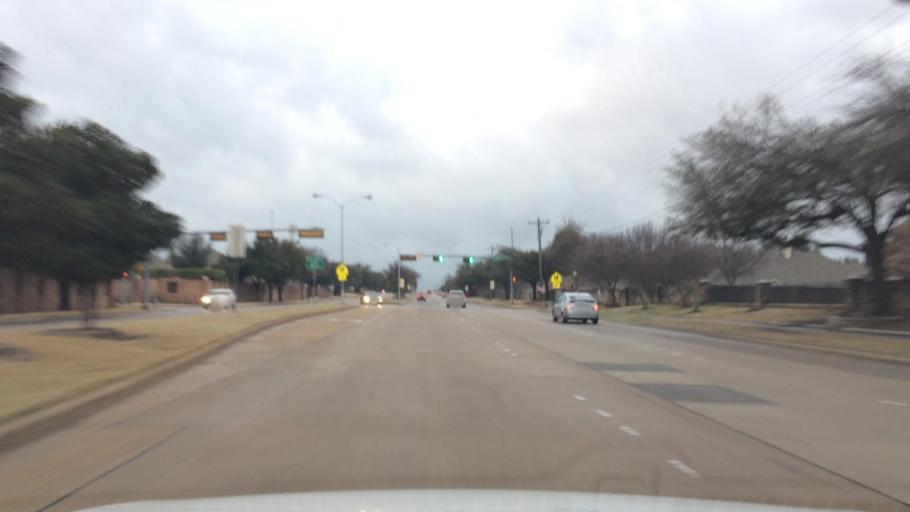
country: US
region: Texas
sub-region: Collin County
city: Frisco
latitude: 33.0940
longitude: -96.7717
